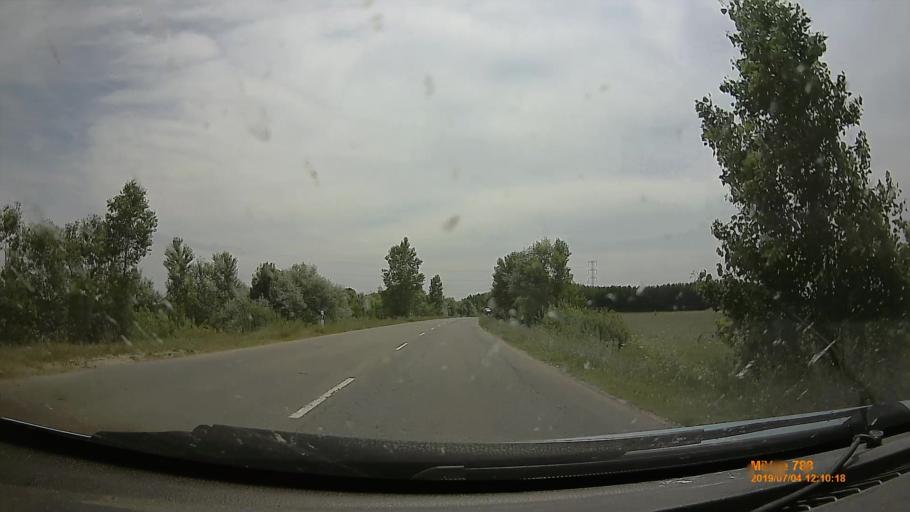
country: HU
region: Pest
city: Gyal
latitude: 47.3848
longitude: 19.2503
